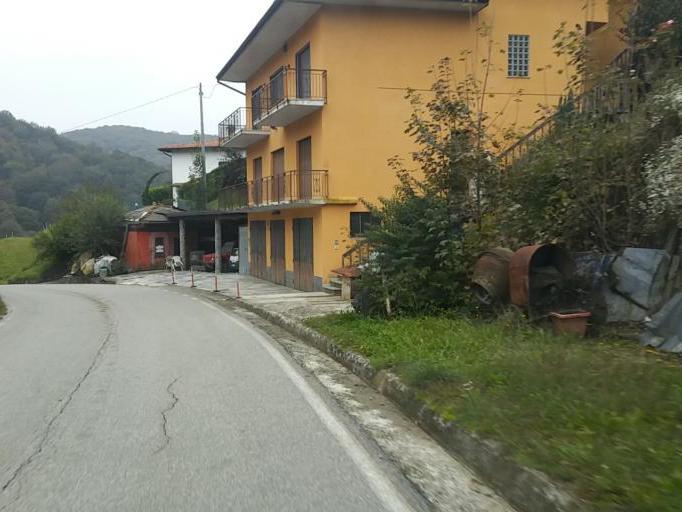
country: IT
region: Piedmont
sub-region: Provincia di Novara
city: Armeno
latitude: 45.8210
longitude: 8.4758
